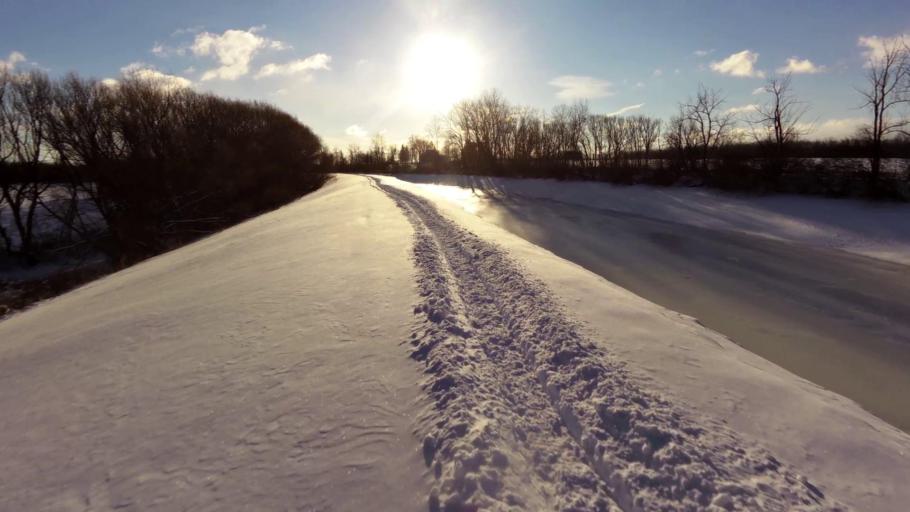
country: US
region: New York
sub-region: Orleans County
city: Albion
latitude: 43.2479
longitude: -78.2817
